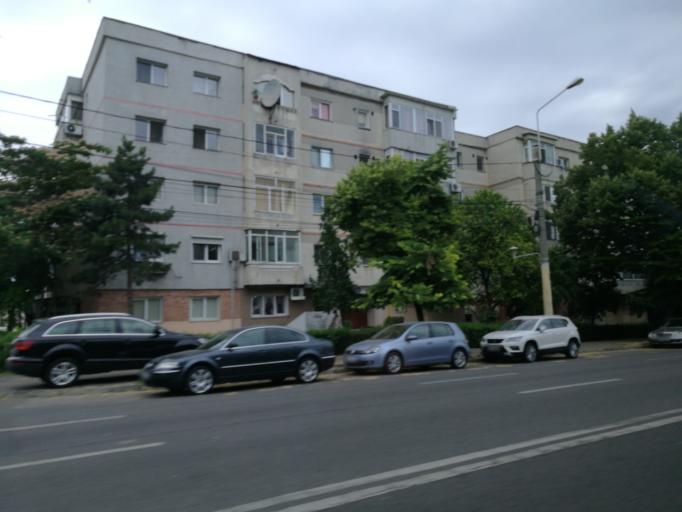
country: RO
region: Constanta
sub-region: Municipiul Constanta
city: Constanta
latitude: 44.1906
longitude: 28.6335
